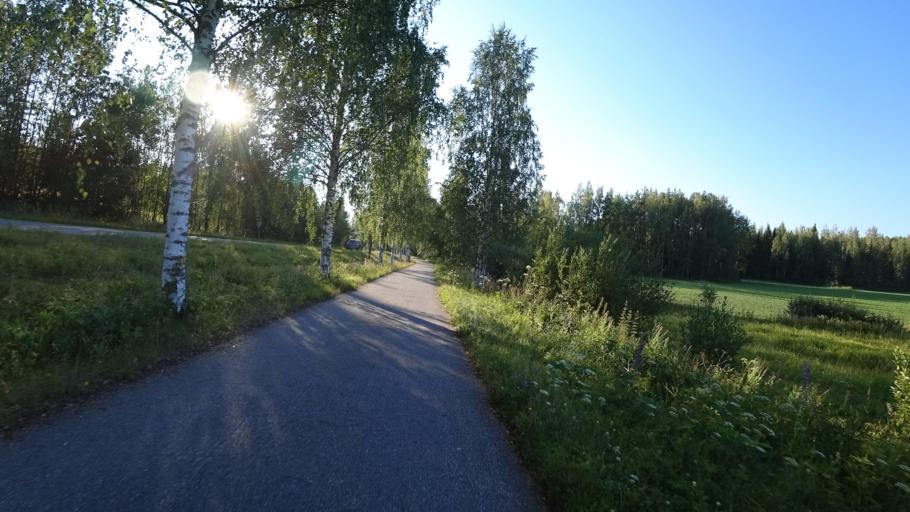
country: FI
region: Pirkanmaa
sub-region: Tampere
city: Nokia
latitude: 61.4724
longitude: 23.3821
